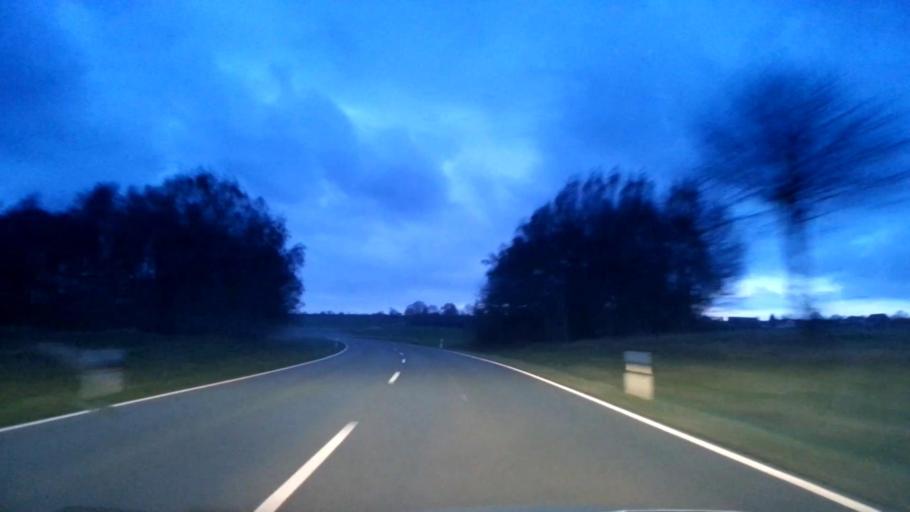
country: DE
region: Bavaria
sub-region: Upper Franconia
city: Kirchenpingarten
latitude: 49.9249
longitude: 11.7907
